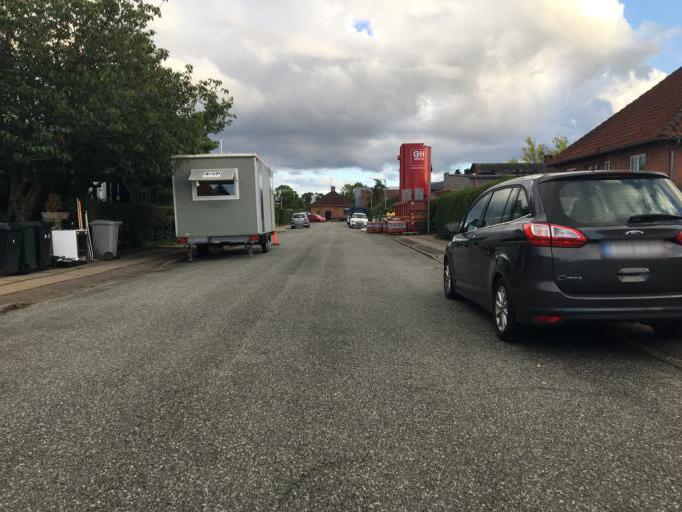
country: DK
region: Capital Region
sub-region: Tarnby Kommune
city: Tarnby
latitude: 55.6345
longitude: 12.6218
